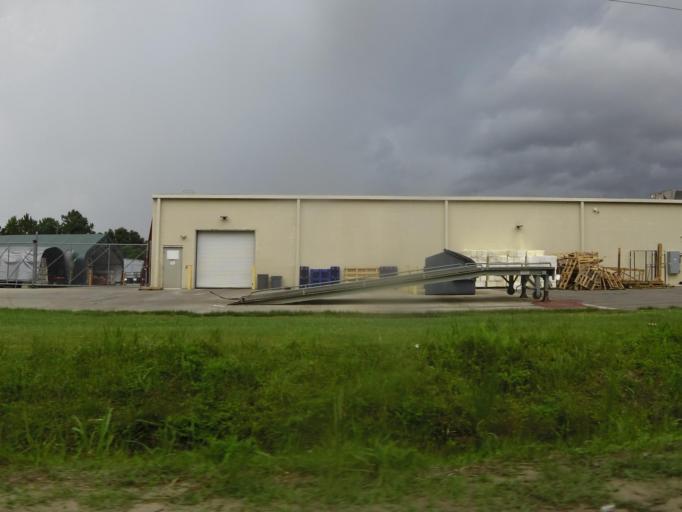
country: US
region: Georgia
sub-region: Camden County
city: Kingsland
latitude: 30.7820
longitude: -81.6407
